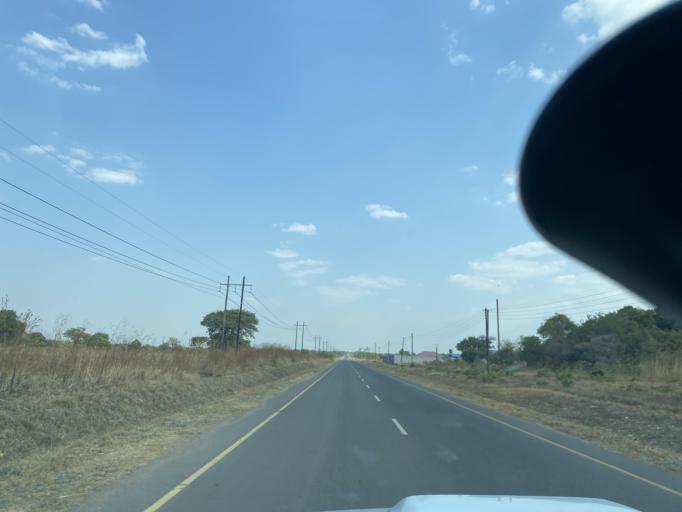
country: ZM
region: Lusaka
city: Lusaka
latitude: -15.3206
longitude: 28.0630
